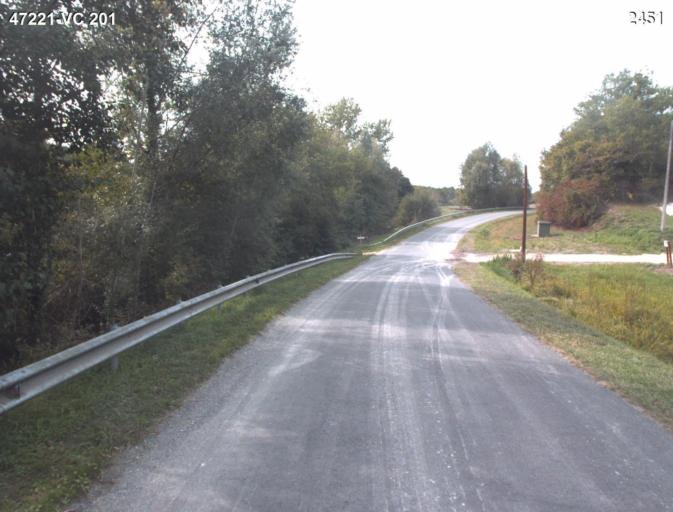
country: FR
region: Aquitaine
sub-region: Departement du Lot-et-Garonne
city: Mezin
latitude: 44.1088
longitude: 0.2479
